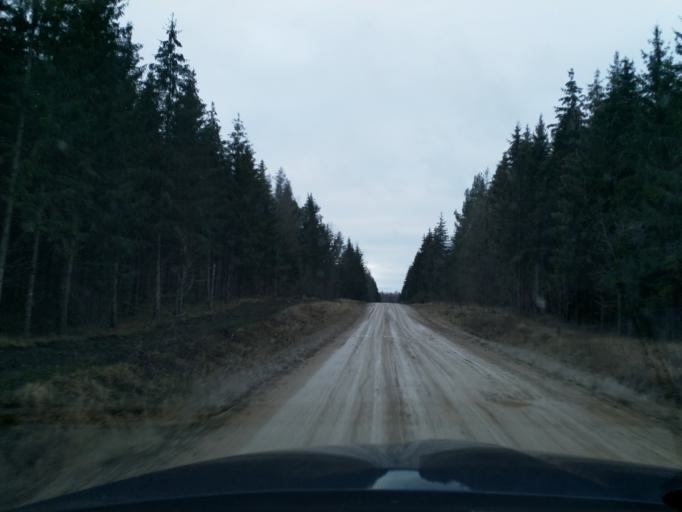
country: LV
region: Kuldigas Rajons
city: Kuldiga
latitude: 56.9040
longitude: 22.2590
